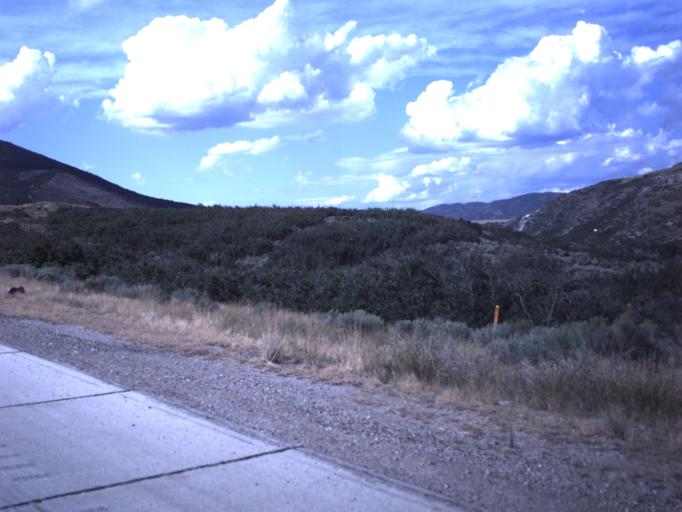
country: US
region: Utah
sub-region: Wasatch County
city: Heber
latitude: 40.5750
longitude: -111.4341
